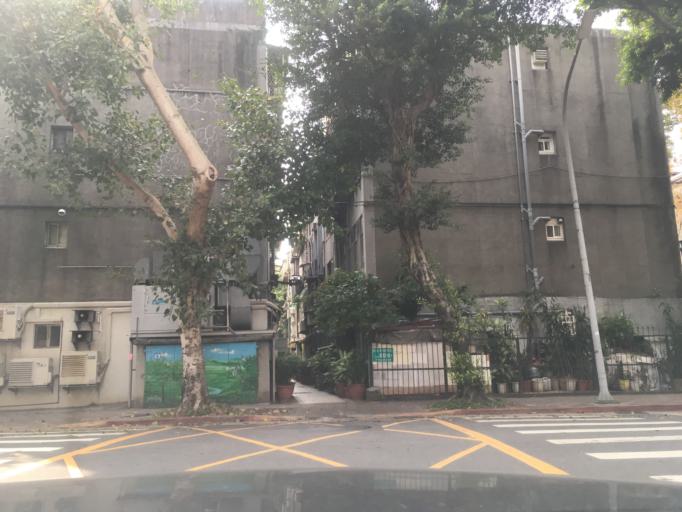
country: TW
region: Taipei
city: Taipei
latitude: 25.0566
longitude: 121.5531
